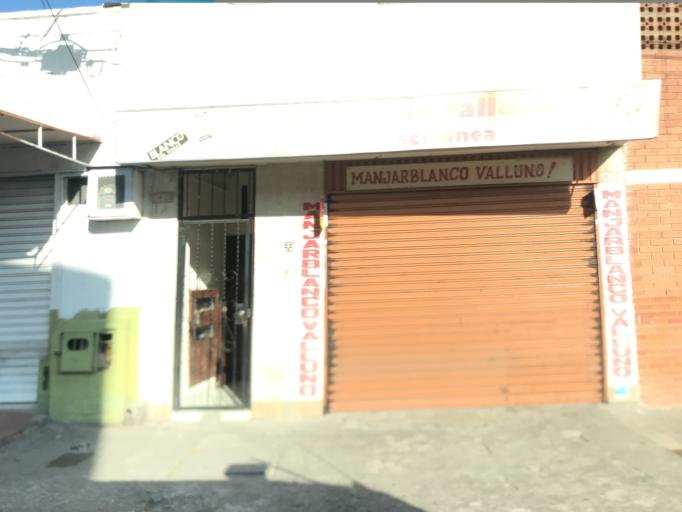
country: CO
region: Valle del Cauca
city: Cali
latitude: 3.4437
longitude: -76.5319
